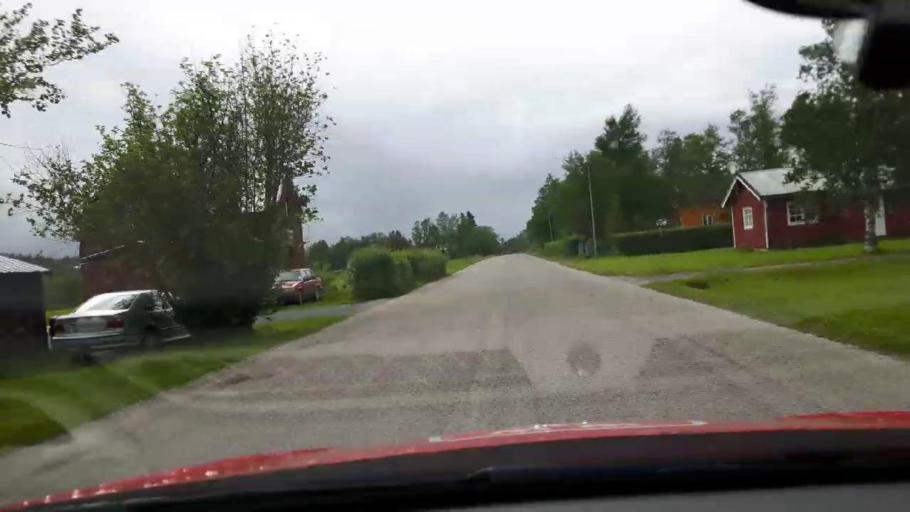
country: SE
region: Jaemtland
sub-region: Are Kommun
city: Are
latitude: 63.2576
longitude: 12.4498
